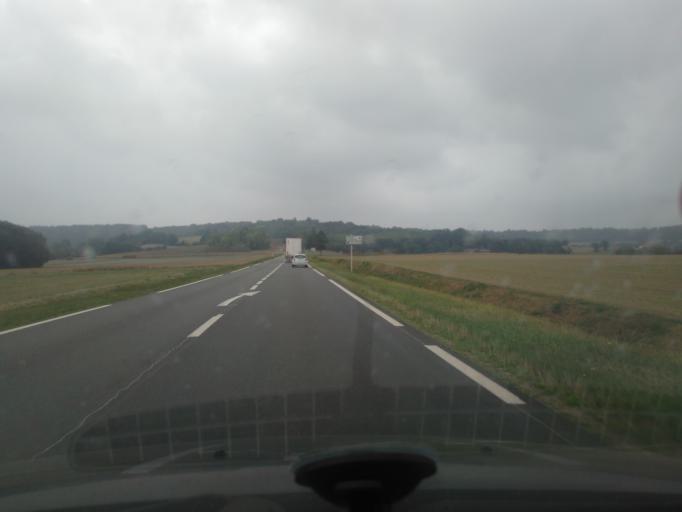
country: FR
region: Picardie
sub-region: Departement de l'Aisne
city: Saint-Erme-Outre-et-Ramecourt
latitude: 49.4827
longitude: 3.7963
